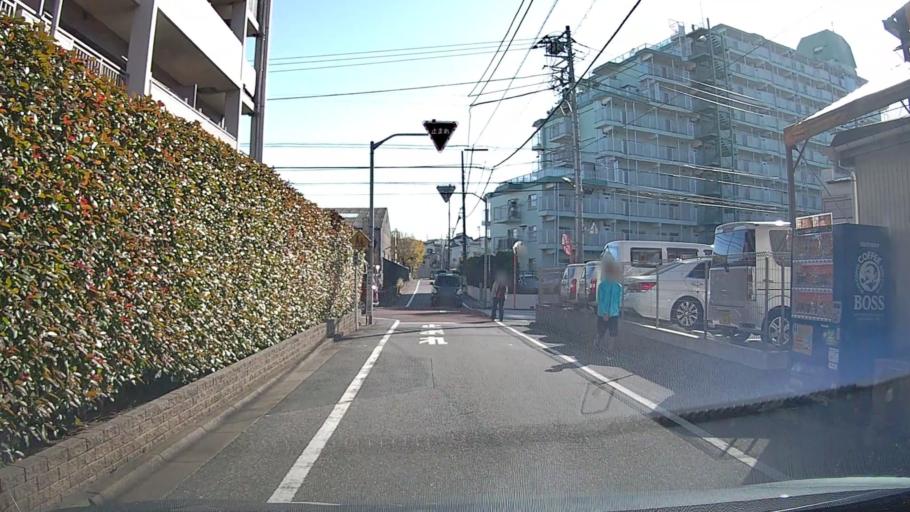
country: JP
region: Saitama
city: Wako
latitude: 35.7436
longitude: 139.6181
